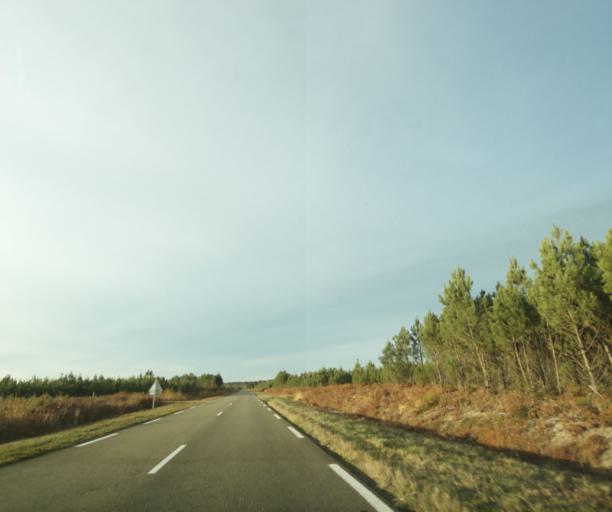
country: FR
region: Aquitaine
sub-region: Departement des Landes
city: Gabarret
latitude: 44.0803
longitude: -0.0709
